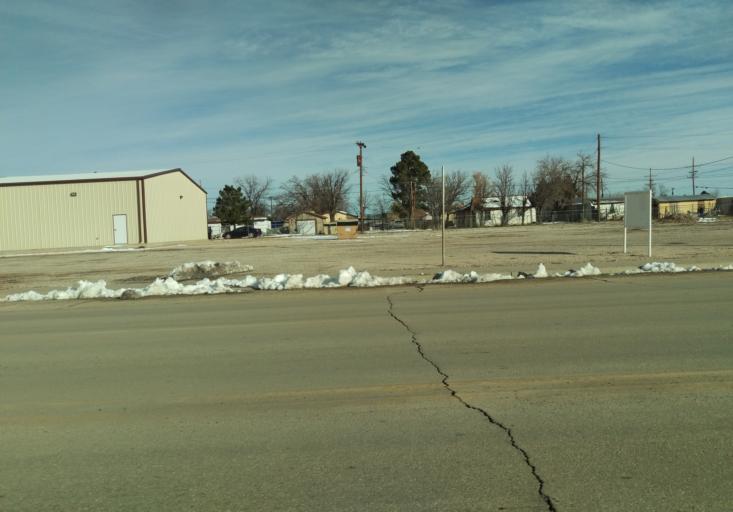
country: US
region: New Mexico
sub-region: Eddy County
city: Carlsbad
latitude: 32.4205
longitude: -104.2445
